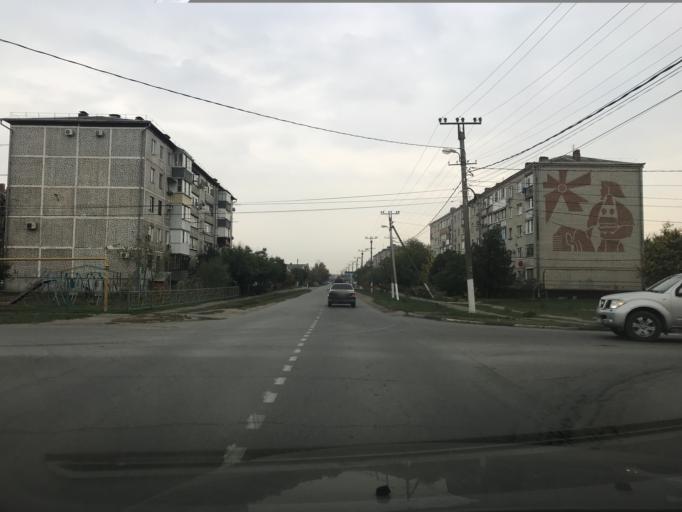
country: RU
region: Krasnodarskiy
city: Slavyansk-na-Kubani
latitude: 45.2668
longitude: 38.1078
